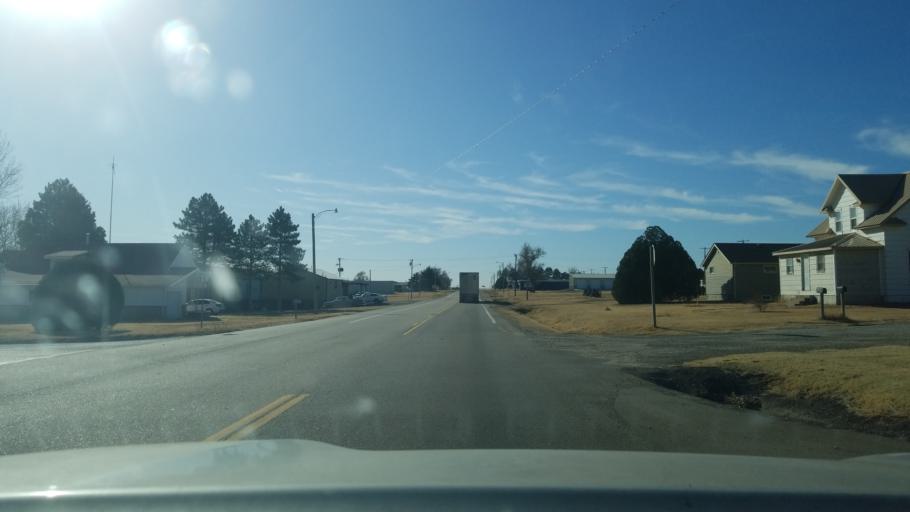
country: US
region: Kansas
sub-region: Ness County
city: Ness City
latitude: 38.4464
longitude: -99.9049
